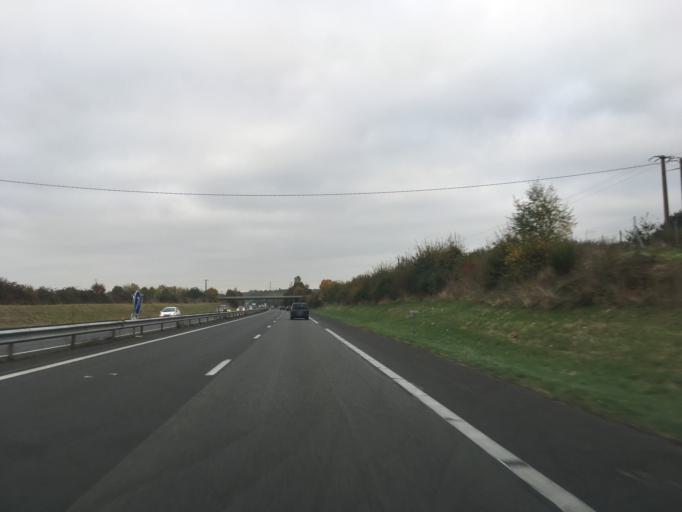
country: FR
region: Pays de la Loire
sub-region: Departement de la Sarthe
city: Noyen-sur-Sarthe
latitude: 47.8342
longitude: -0.1376
